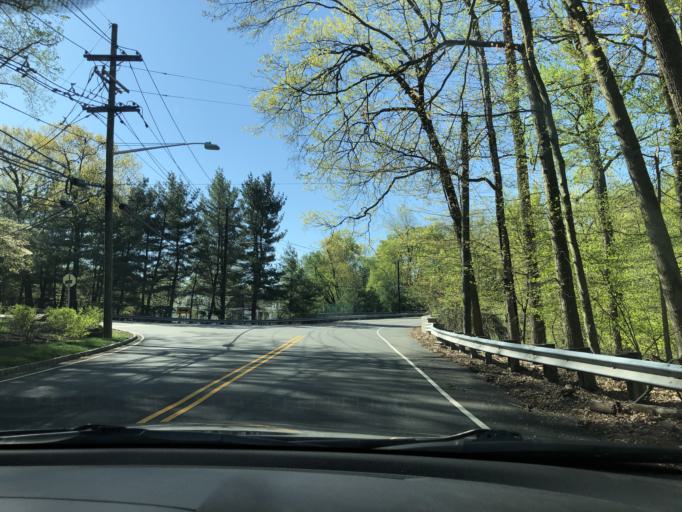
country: US
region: New Jersey
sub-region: Essex County
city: North Caldwell
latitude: 40.8678
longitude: -74.2646
